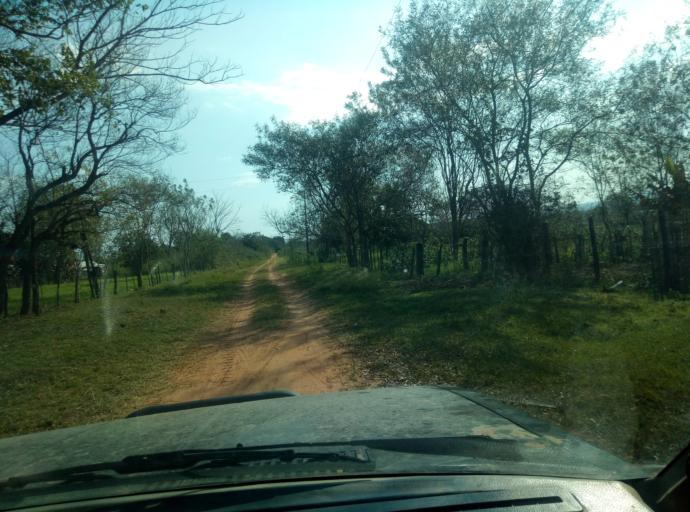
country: PY
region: Caaguazu
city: Doctor Cecilio Baez
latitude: -25.1430
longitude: -56.2496
